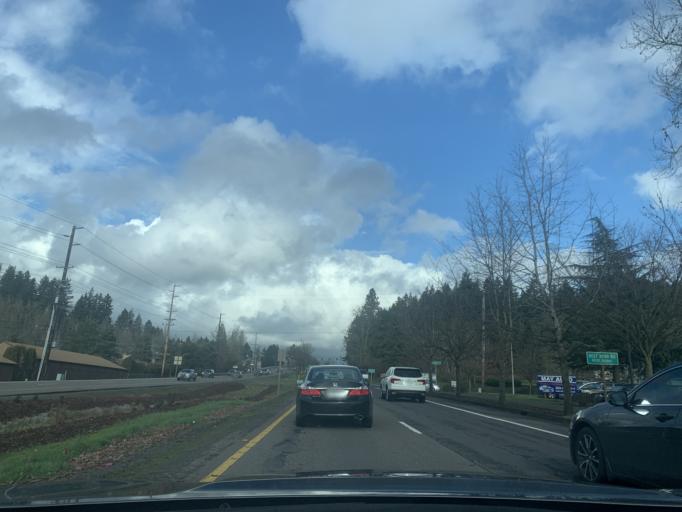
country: US
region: Oregon
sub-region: Washington County
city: King City
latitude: 45.4092
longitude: -122.7943
